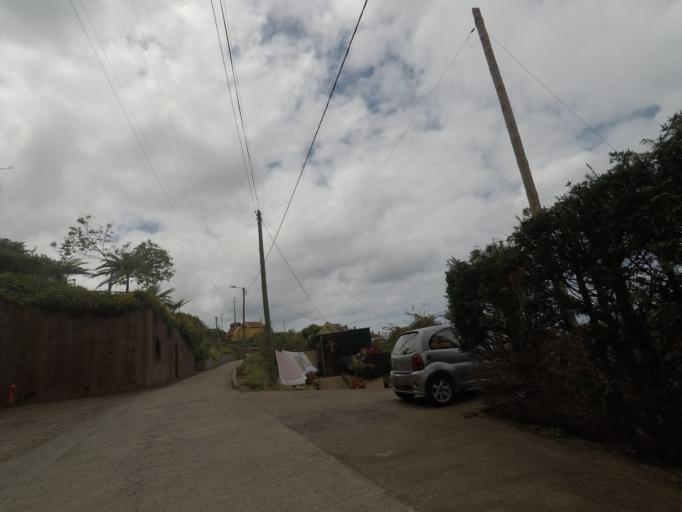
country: PT
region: Madeira
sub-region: Santana
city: Santana
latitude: 32.8022
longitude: -16.8730
